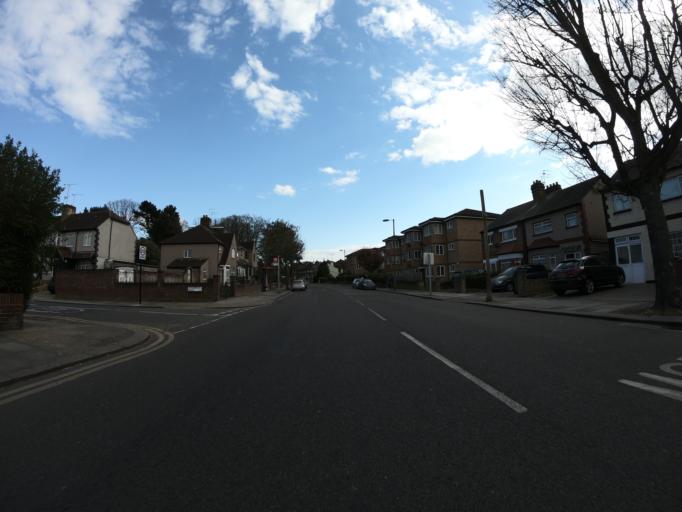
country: GB
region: England
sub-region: Greater London
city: Abbey Wood
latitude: 51.4764
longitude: 0.1082
